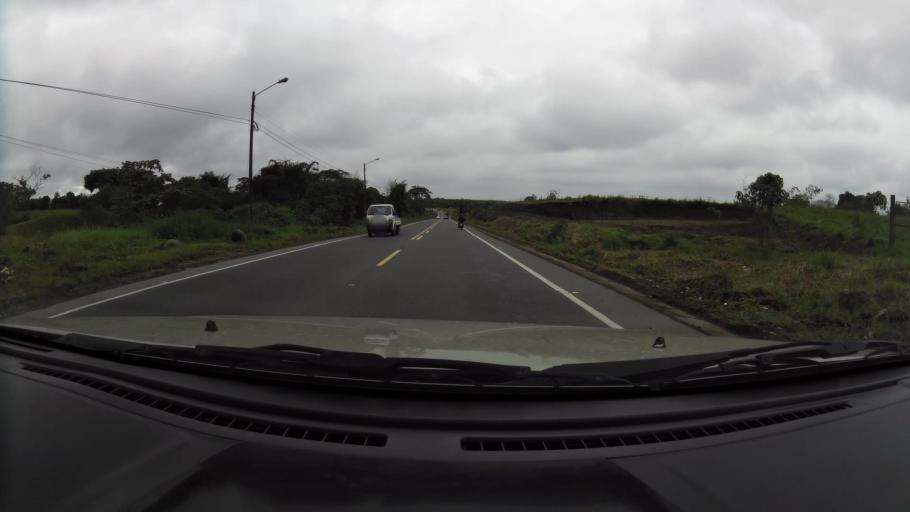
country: EC
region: Santo Domingo de los Tsachilas
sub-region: Canton Santo Domingo de los Colorados
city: Santo Domingo de los Colorados
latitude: -0.2605
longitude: -79.1280
